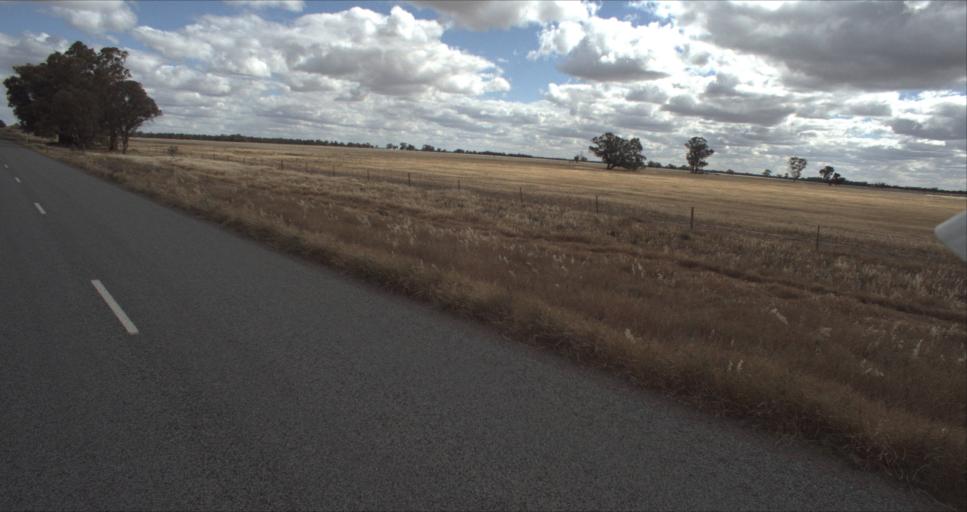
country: AU
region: New South Wales
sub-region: Leeton
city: Leeton
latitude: -34.6703
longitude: 146.3476
